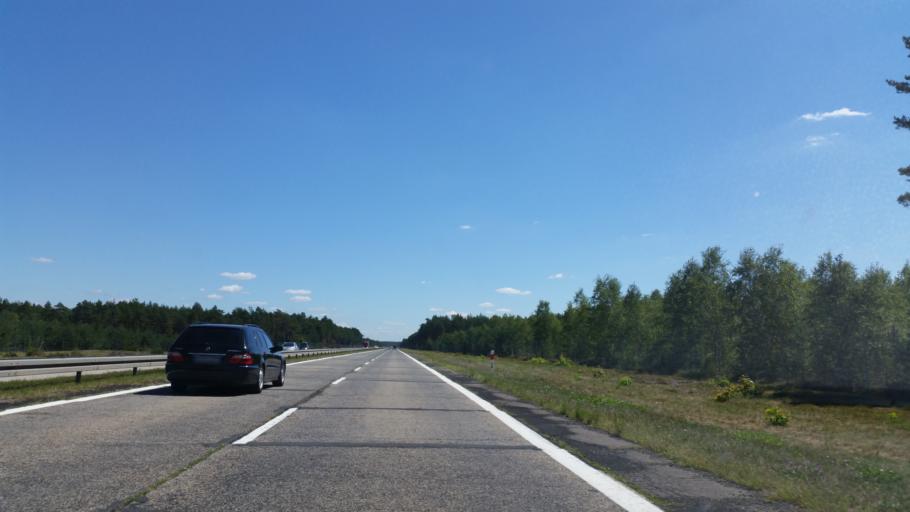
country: PL
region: Lubusz
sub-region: Powiat zaganski
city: Malomice
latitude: 51.4282
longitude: 15.4248
